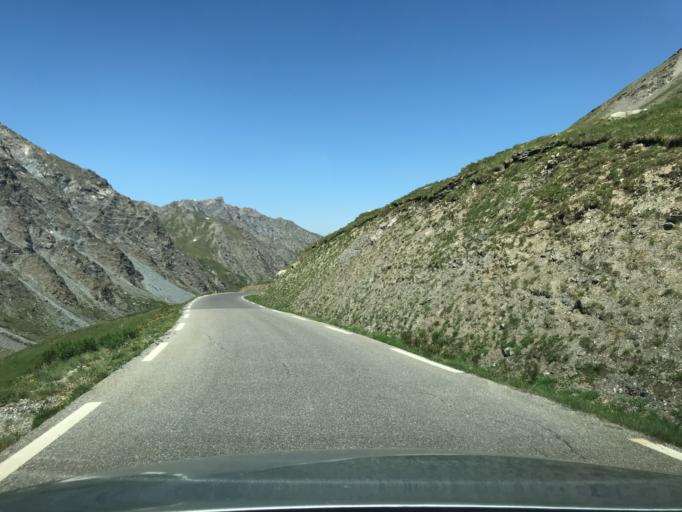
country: IT
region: Piedmont
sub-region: Provincia di Cuneo
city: Pontechianale
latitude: 44.6919
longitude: 6.9704
